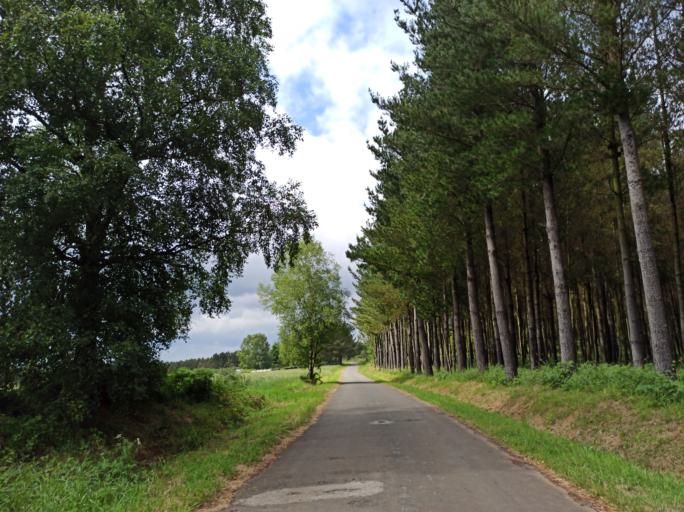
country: ES
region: Galicia
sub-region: Provincia de Pontevedra
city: Silleda
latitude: 42.7624
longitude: -8.1601
